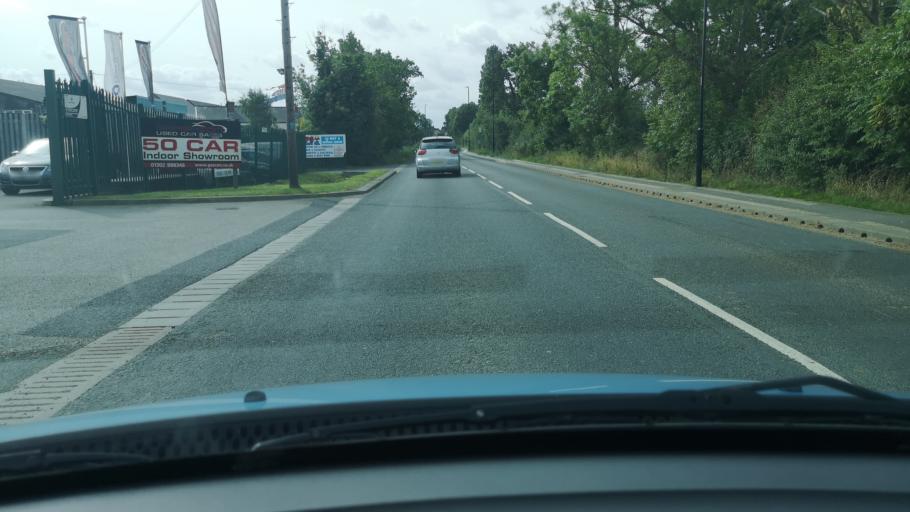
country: GB
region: England
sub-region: Doncaster
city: Kirk Sandall
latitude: 53.5689
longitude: -1.0666
